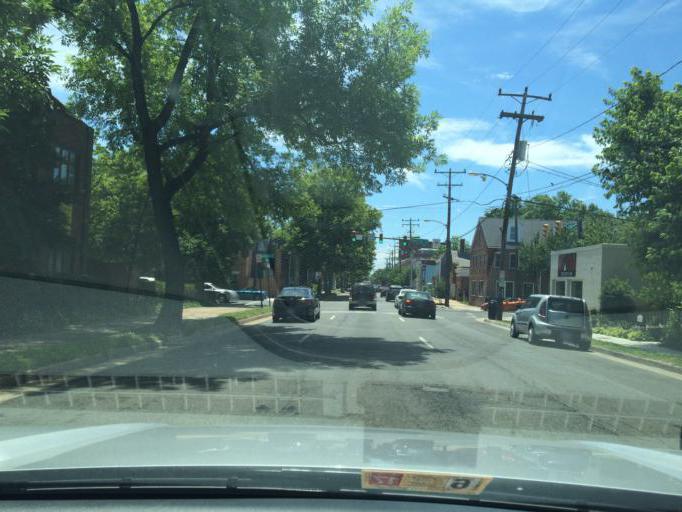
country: US
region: Virginia
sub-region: City of Alexandria
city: Alexandria
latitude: 38.8095
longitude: -77.0505
